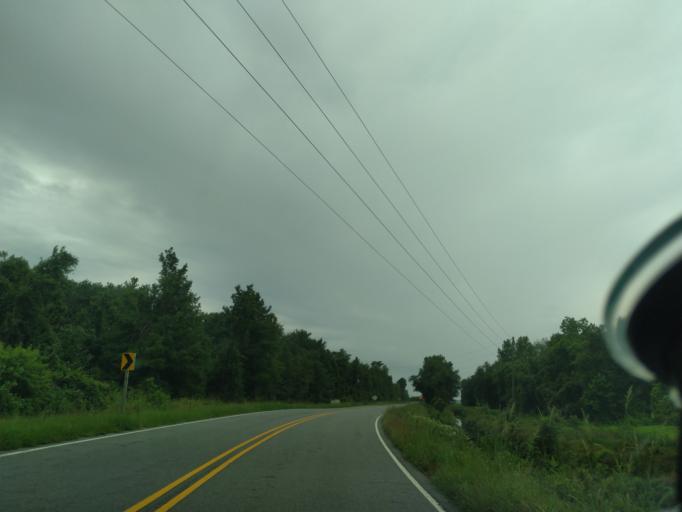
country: US
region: North Carolina
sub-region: Washington County
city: Plymouth
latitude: 35.7878
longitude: -76.5189
